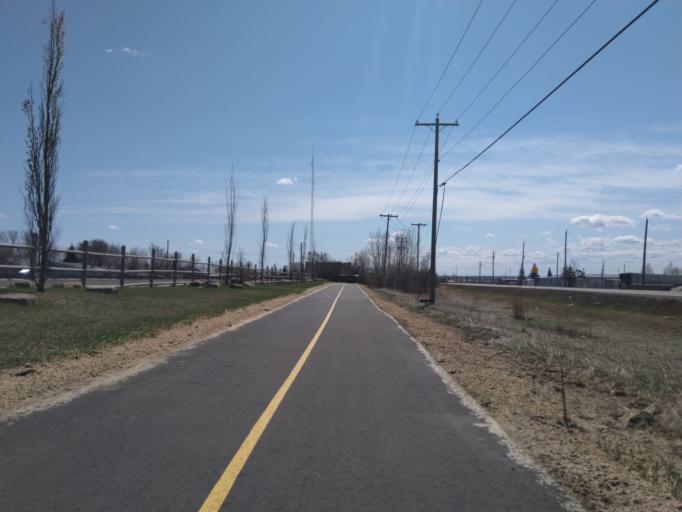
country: CA
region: Alberta
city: Chestermere
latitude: 50.9548
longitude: -113.9116
